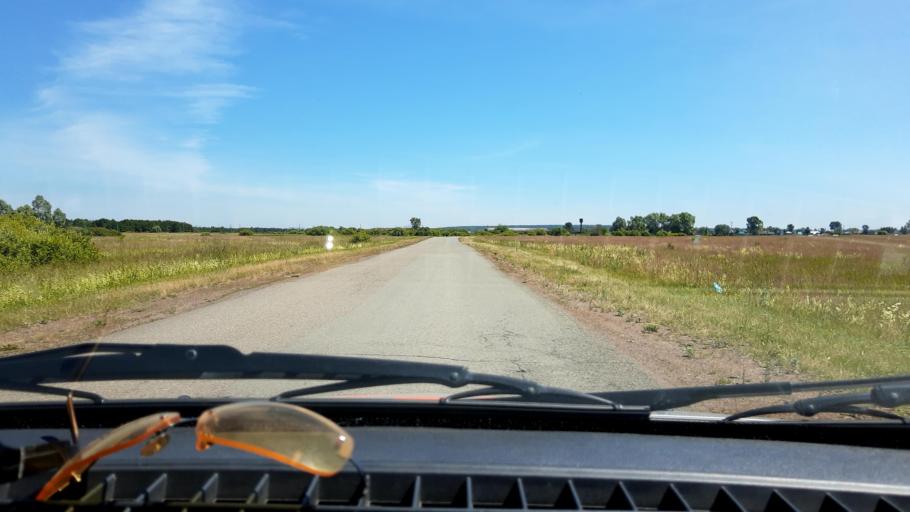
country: RU
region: Bashkortostan
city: Mikhaylovka
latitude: 54.9765
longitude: 55.7781
